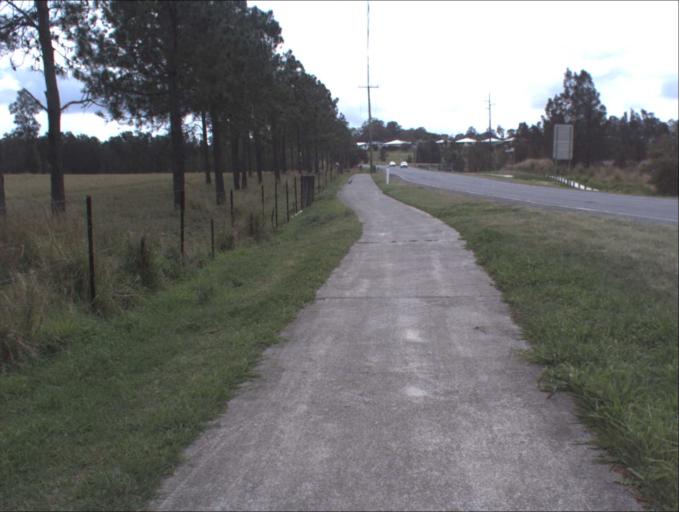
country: AU
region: Queensland
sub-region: Logan
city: Waterford West
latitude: -27.6966
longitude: 153.1179
